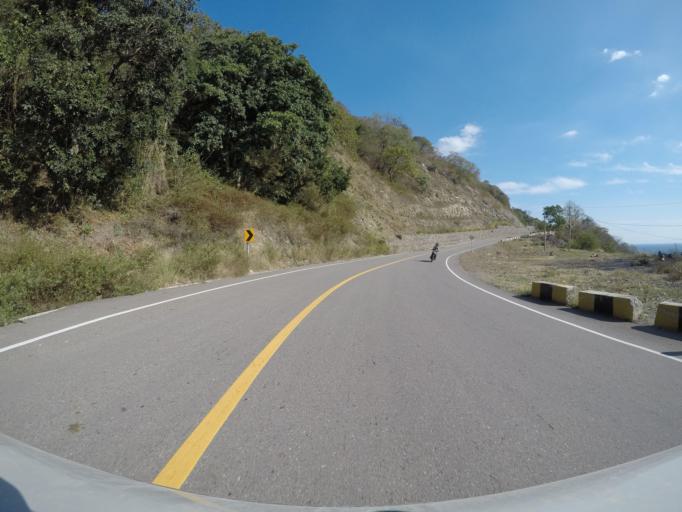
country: TL
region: Liquica
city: Maubara
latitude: -8.6478
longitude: 125.1229
